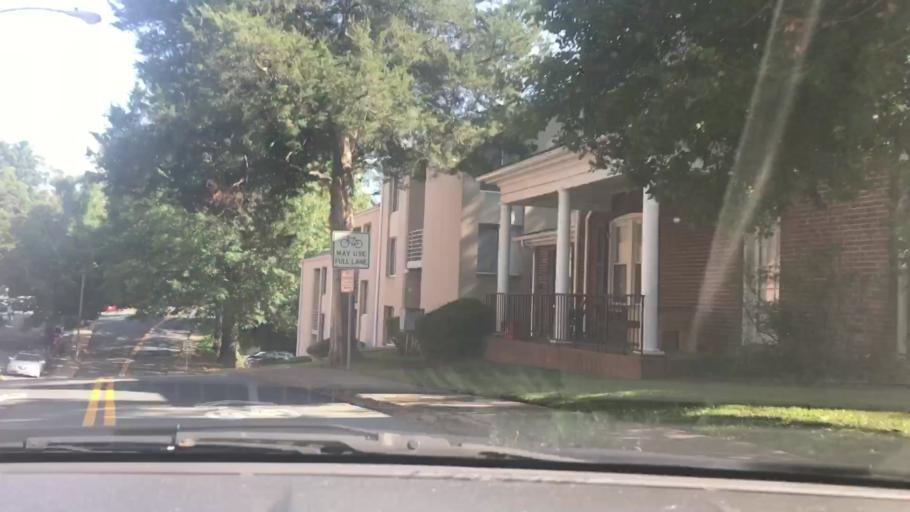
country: US
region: Virginia
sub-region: City of Charlottesville
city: Charlottesville
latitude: 38.0276
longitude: -78.5113
